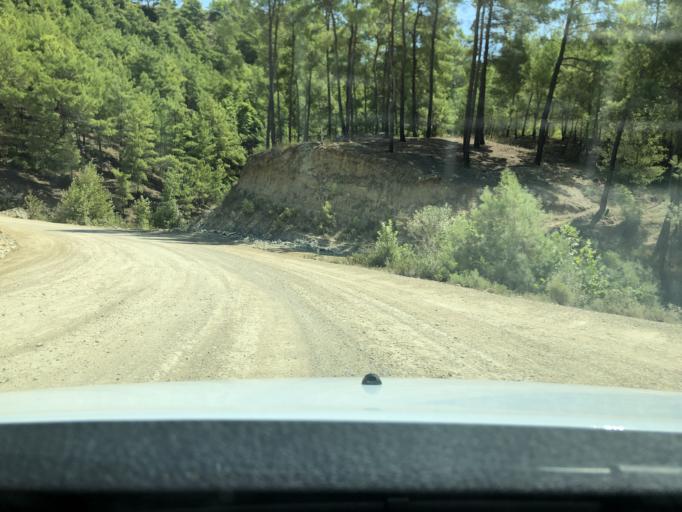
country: TR
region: Antalya
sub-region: Manavgat
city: Manavgat
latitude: 36.8325
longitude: 31.5325
